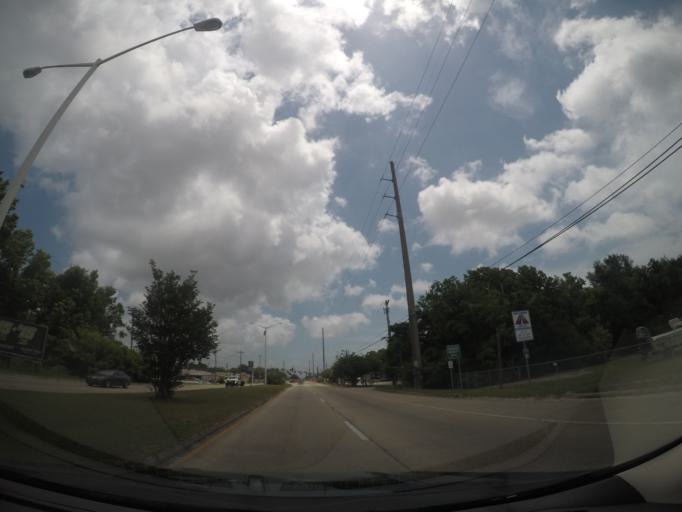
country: US
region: Mississippi
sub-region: Hancock County
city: Waveland
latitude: 30.3097
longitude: -89.3675
